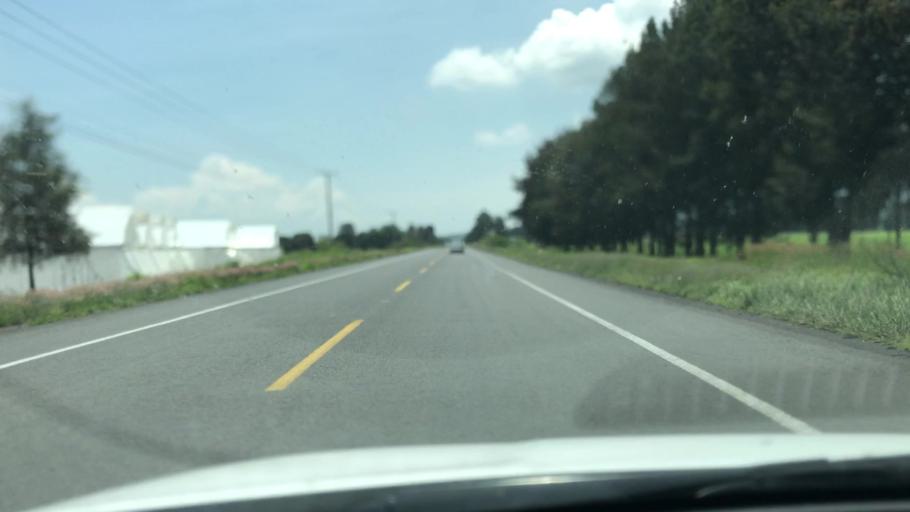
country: MX
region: Michoacan
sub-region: Yurecuaro
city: Yurecuaro
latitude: 20.3392
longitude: -102.1815
